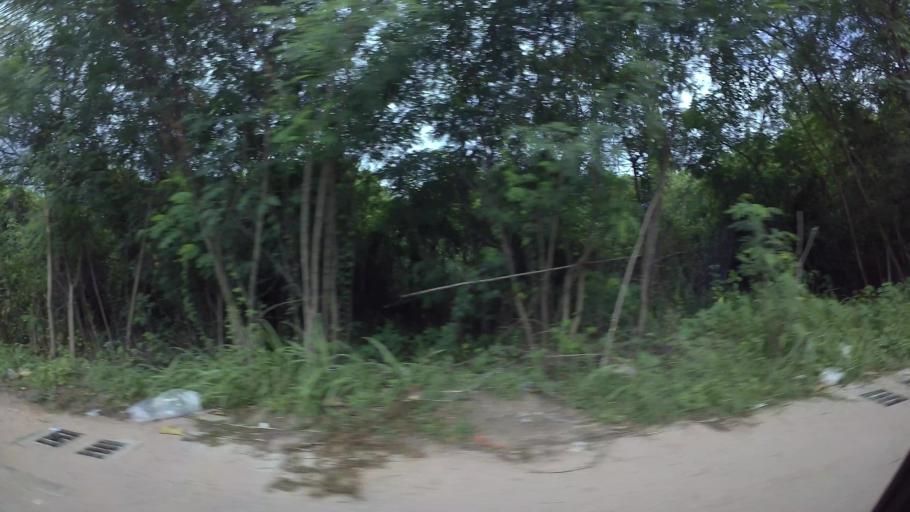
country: TH
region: Chon Buri
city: Si Racha
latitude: 13.1472
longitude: 100.9776
